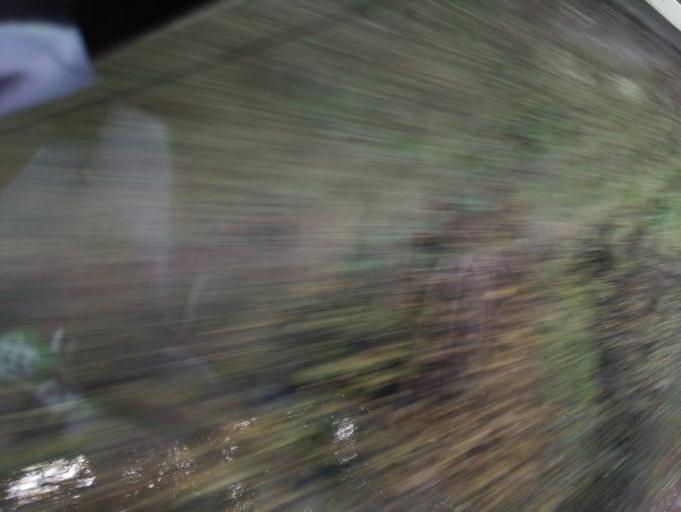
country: GB
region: England
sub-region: Wiltshire
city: Chicklade
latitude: 51.1265
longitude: -2.1632
